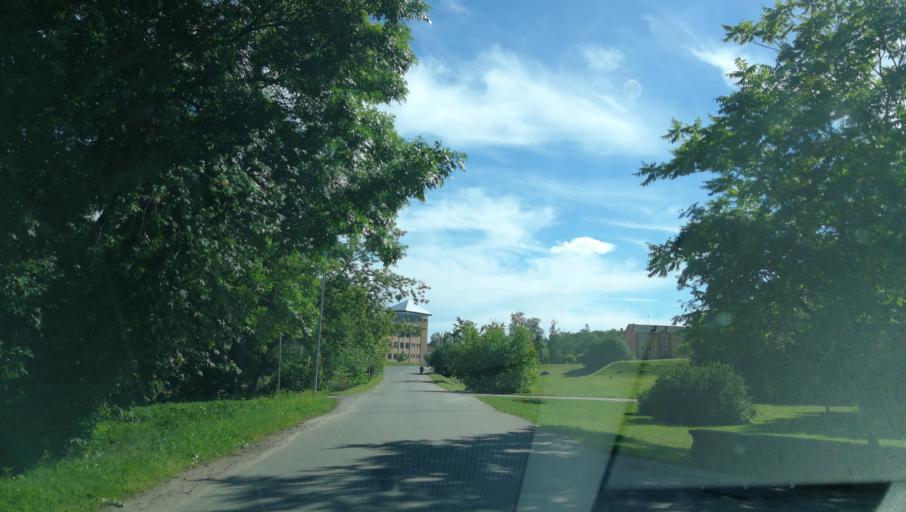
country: LV
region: Cesvaine
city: Cesvaine
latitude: 56.9686
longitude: 26.3169
